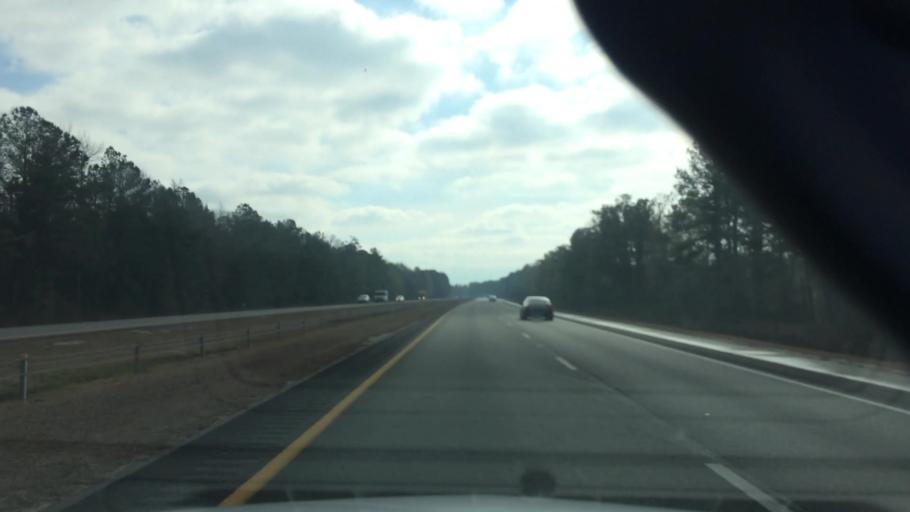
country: US
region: North Carolina
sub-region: Pender County
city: Burgaw
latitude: 34.5459
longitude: -77.8934
